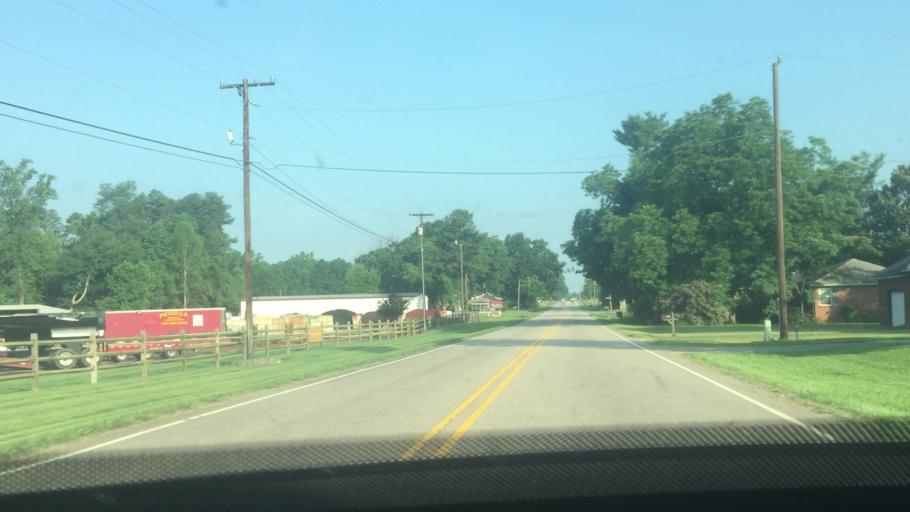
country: US
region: North Carolina
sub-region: Iredell County
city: Mooresville
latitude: 35.5832
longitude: -80.7391
